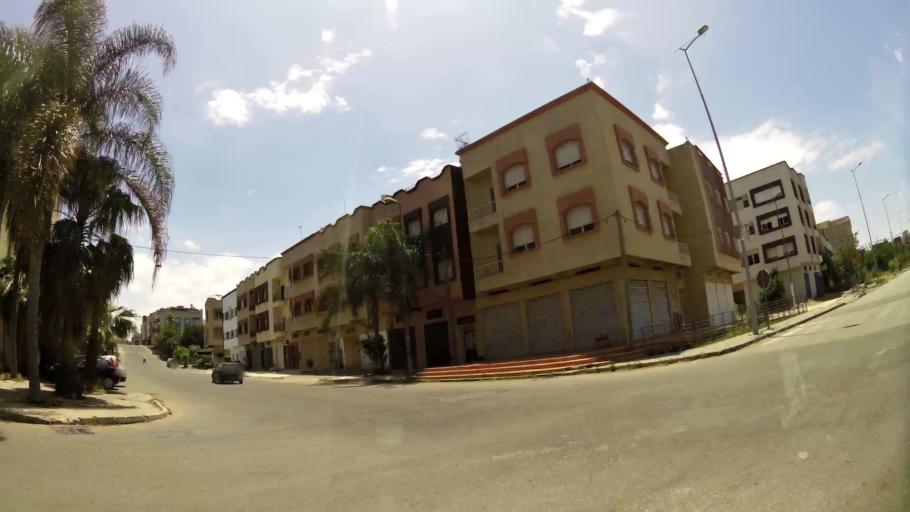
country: MA
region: Gharb-Chrarda-Beni Hssen
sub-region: Kenitra Province
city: Kenitra
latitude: 34.2545
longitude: -6.6095
